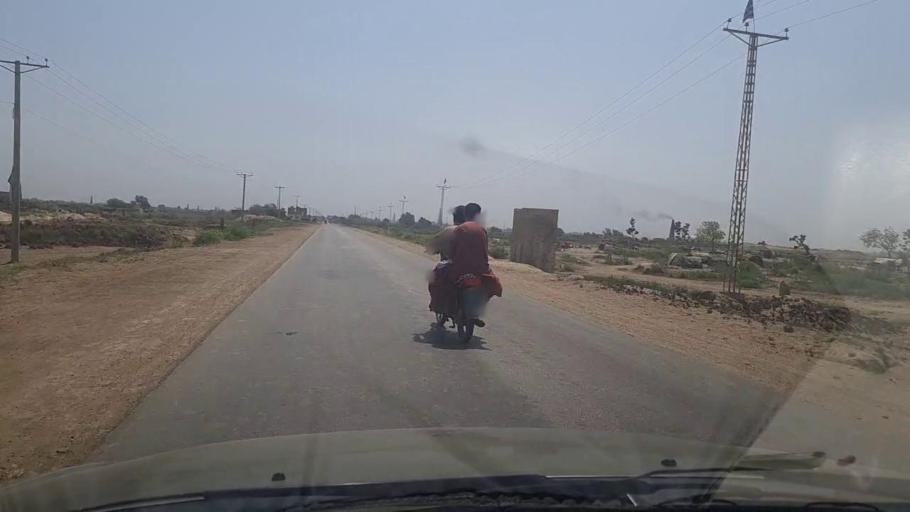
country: PK
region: Sindh
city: Hyderabad
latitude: 25.3846
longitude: 68.4366
